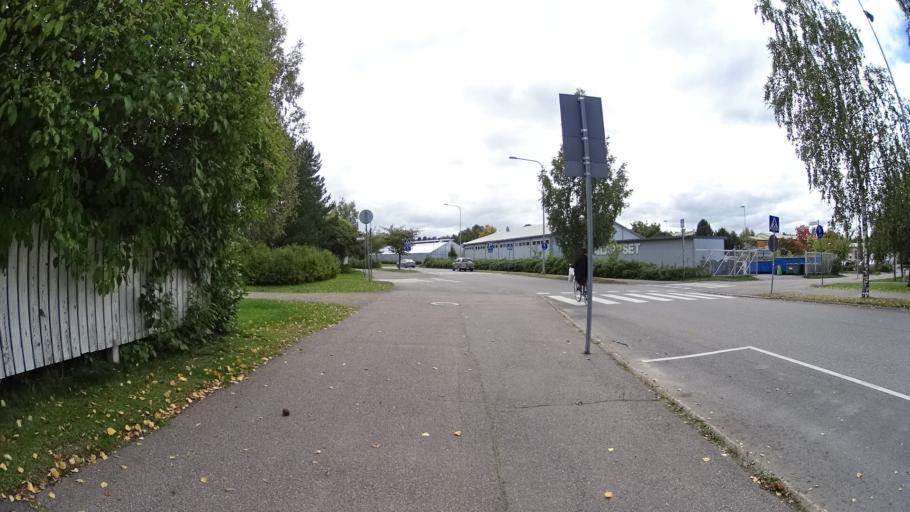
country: FI
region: Uusimaa
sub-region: Helsinki
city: Helsinki
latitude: 60.2591
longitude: 24.9440
